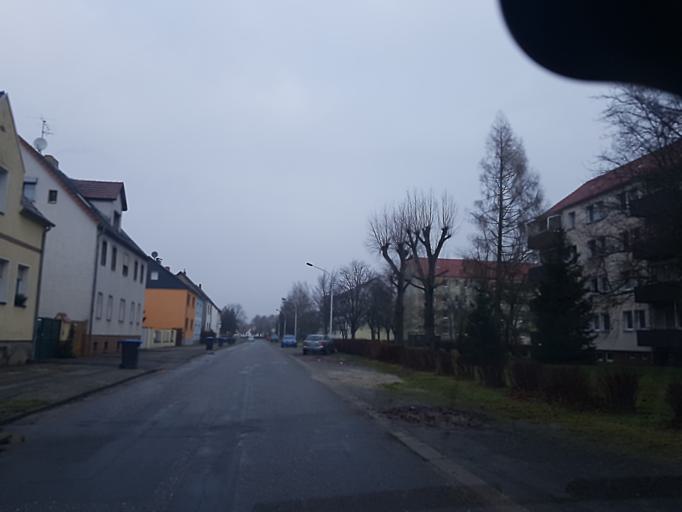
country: DE
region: Brandenburg
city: Finsterwalde
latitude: 51.6200
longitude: 13.7063
